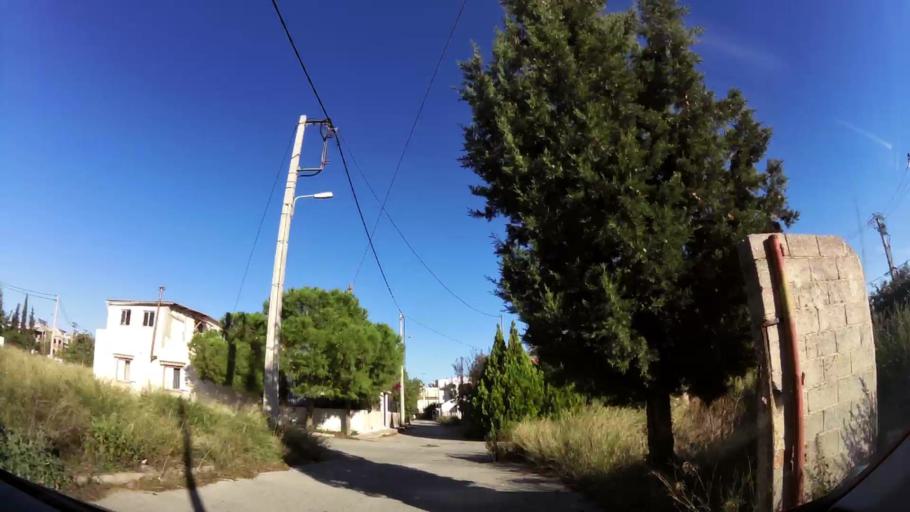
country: GR
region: Attica
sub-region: Nomarchia Anatolikis Attikis
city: Acharnes
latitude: 38.0912
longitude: 23.7224
